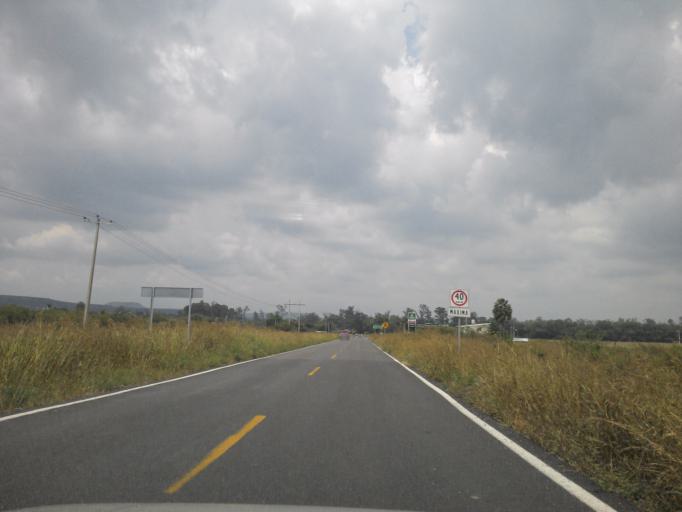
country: MX
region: Jalisco
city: San Diego de Alejandria
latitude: 20.8698
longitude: -101.9889
